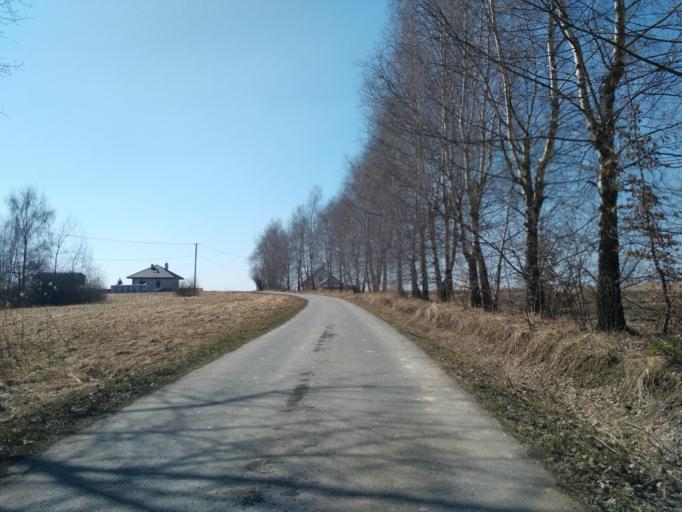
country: PL
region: Subcarpathian Voivodeship
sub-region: Powiat strzyzowski
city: Czudec
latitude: 49.9641
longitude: 21.8294
